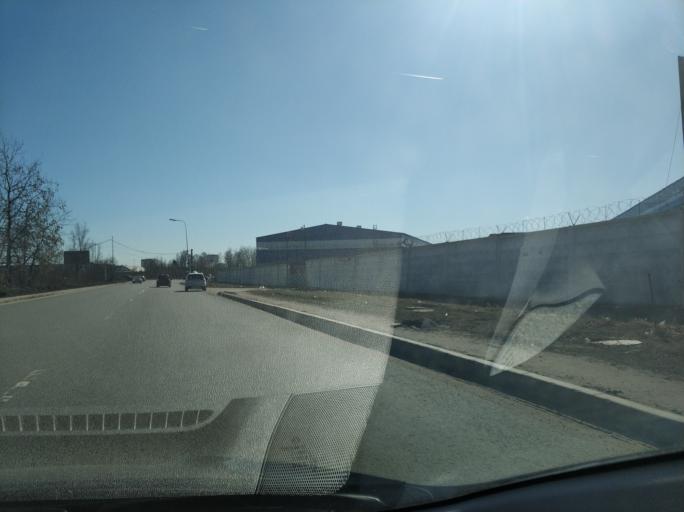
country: RU
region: Leningrad
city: Bugry
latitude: 60.0623
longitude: 30.3847
